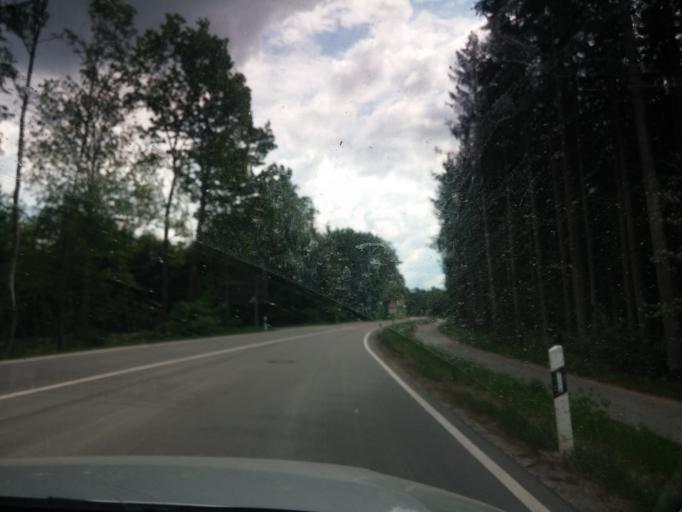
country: DE
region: Bavaria
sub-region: Upper Bavaria
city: Hohenkirchen-Siegertsbrunn
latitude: 48.0069
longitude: 11.7090
